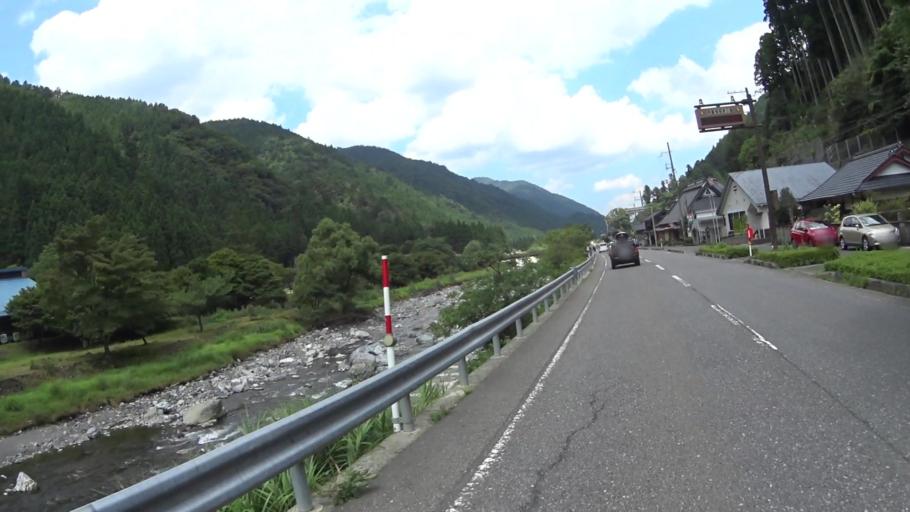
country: JP
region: Shiga Prefecture
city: Kitahama
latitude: 35.2439
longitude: 135.8667
